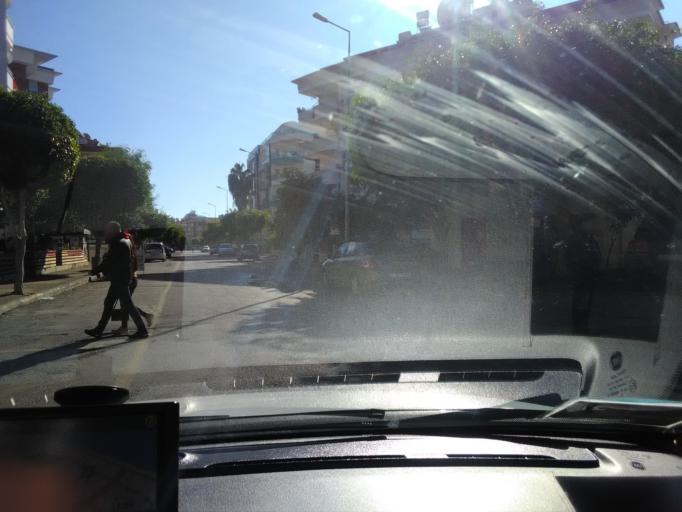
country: TR
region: Antalya
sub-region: Alanya
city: Alanya
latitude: 36.5341
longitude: 32.0431
